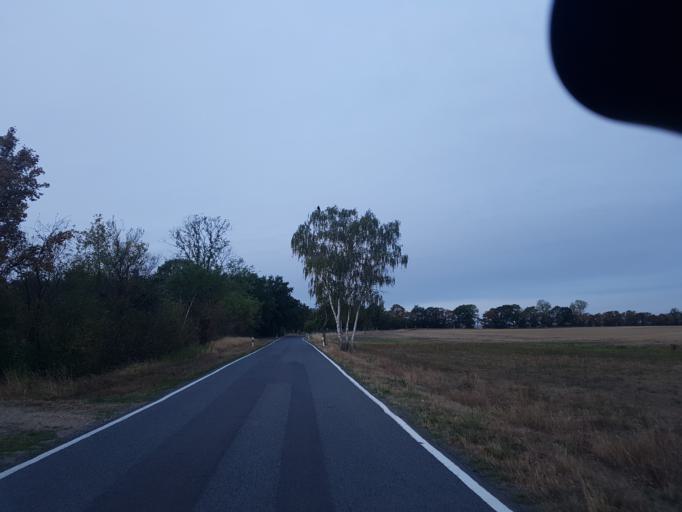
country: DE
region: Brandenburg
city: Muhlberg
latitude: 51.4957
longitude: 13.2650
